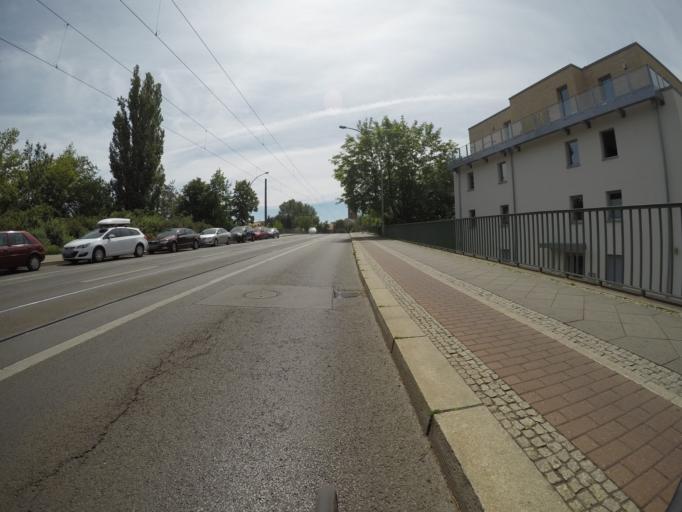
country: DE
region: Berlin
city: Kopenick Bezirk
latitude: 52.4493
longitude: 13.5740
